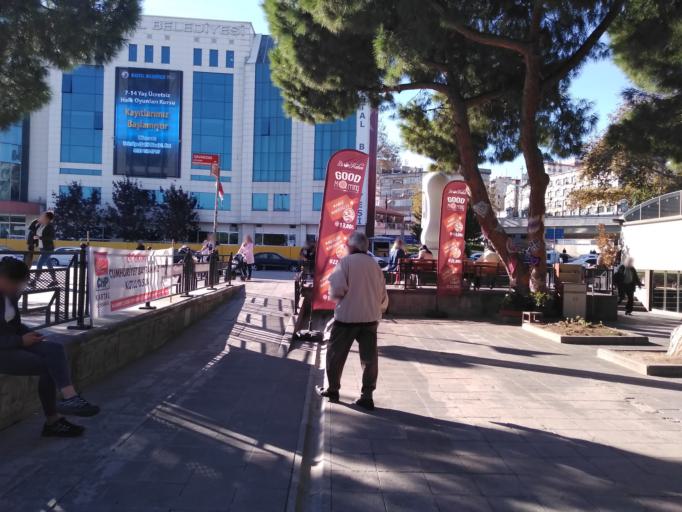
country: TR
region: Istanbul
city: Maltepe
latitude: 40.8884
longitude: 29.1862
